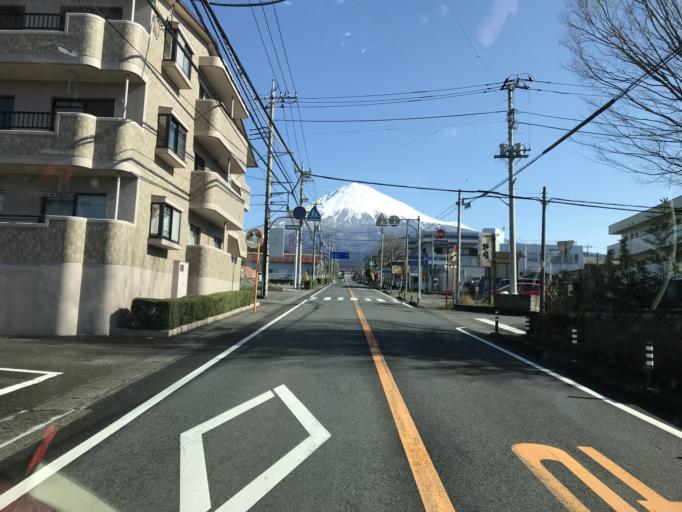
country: JP
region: Shizuoka
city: Fujinomiya
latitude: 35.2459
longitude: 138.6242
